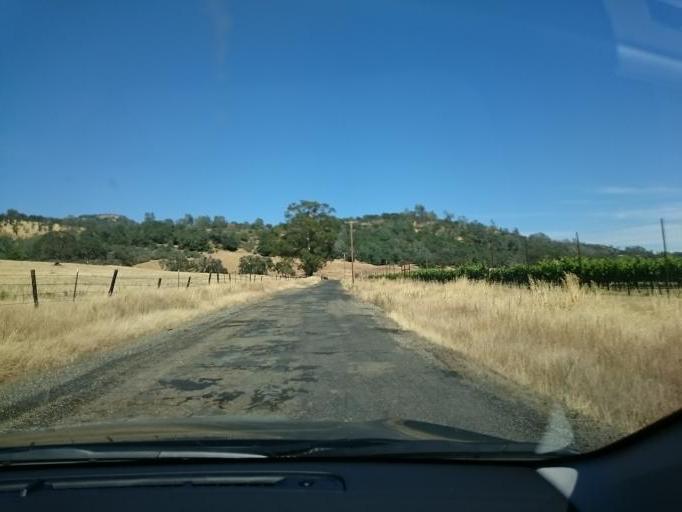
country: US
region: California
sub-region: Calaveras County
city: Copperopolis
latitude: 38.0487
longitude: -120.6954
